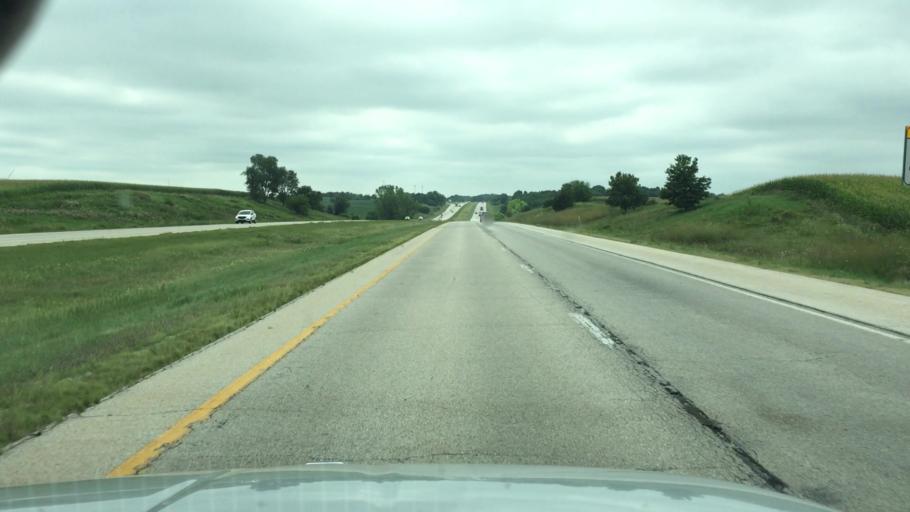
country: US
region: Illinois
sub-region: Henry County
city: Orion
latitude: 41.2280
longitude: -90.3319
